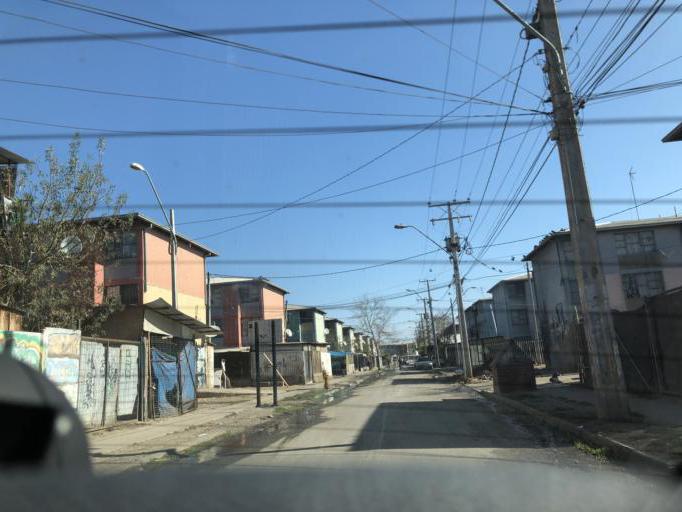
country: CL
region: Santiago Metropolitan
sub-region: Provincia de Cordillera
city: Puente Alto
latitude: -33.6270
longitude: -70.6174
